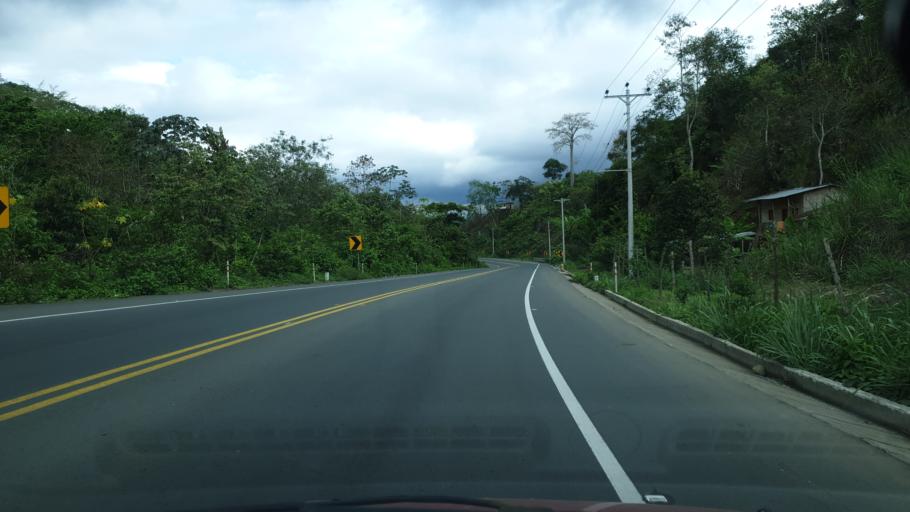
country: EC
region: Manabi
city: Pajan
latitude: -1.5632
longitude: -80.5233
